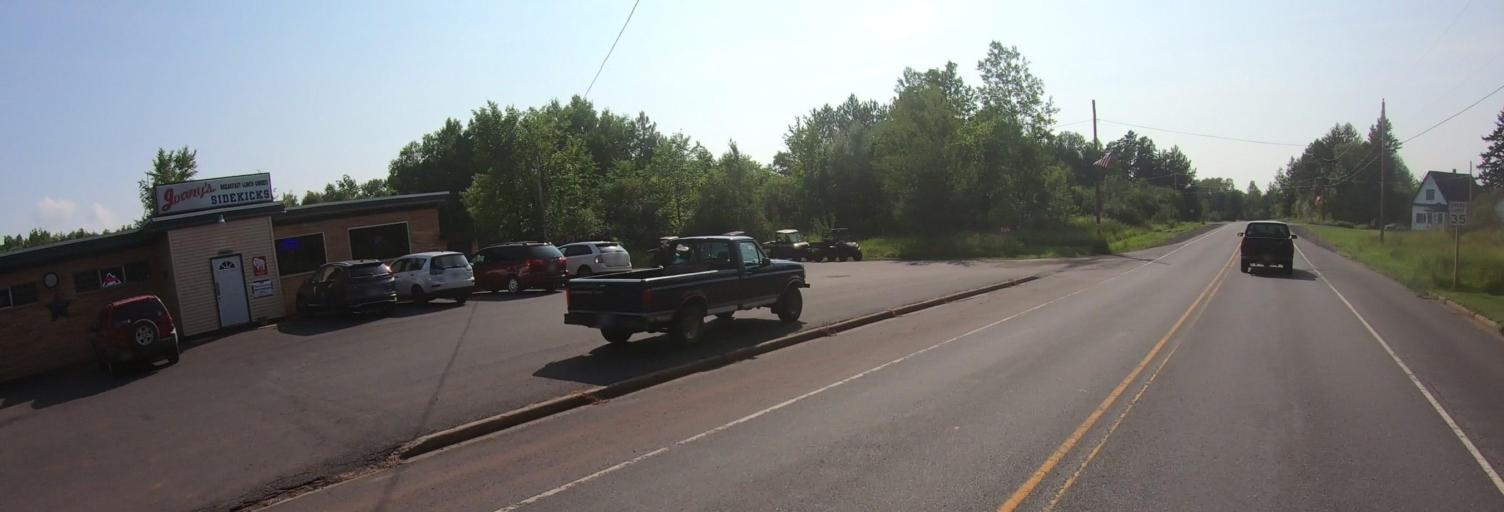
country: US
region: Wisconsin
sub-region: Iron County
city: Hurley
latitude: 46.4008
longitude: -90.3257
